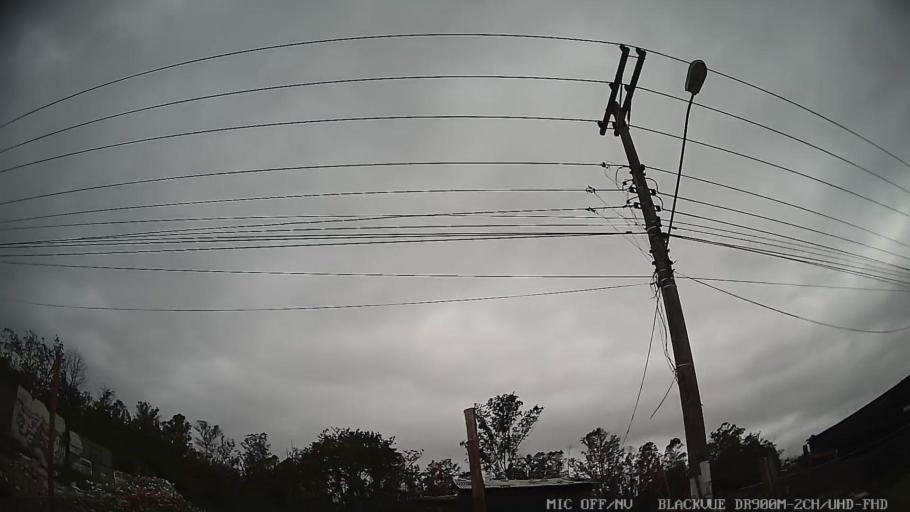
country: BR
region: Sao Paulo
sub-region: Itaquaquecetuba
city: Itaquaquecetuba
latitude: -23.4848
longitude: -46.4013
